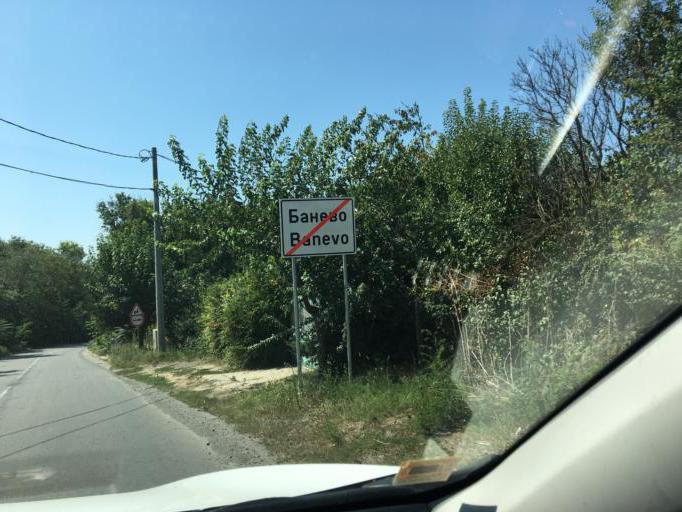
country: BG
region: Burgas
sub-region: Obshtina Kameno
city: Kameno
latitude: 42.6204
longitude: 27.3950
